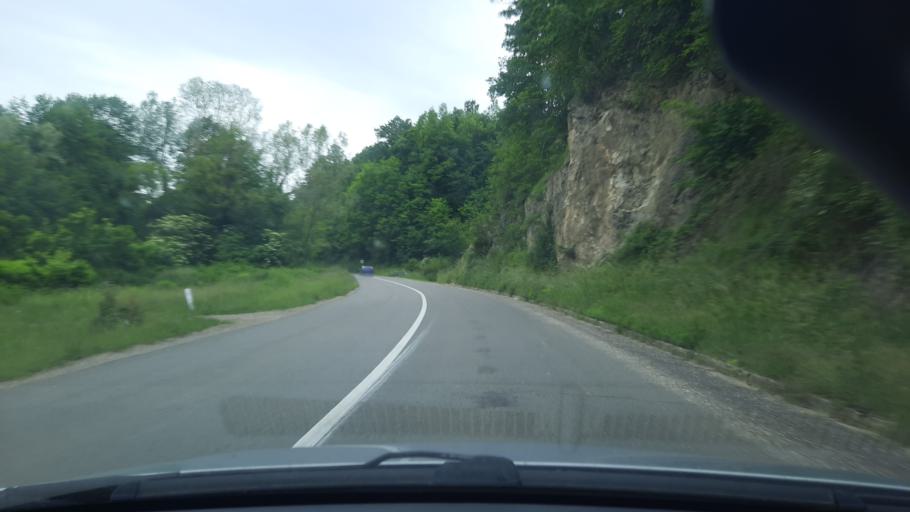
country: RS
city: Bukor
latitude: 44.5088
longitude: 19.4980
